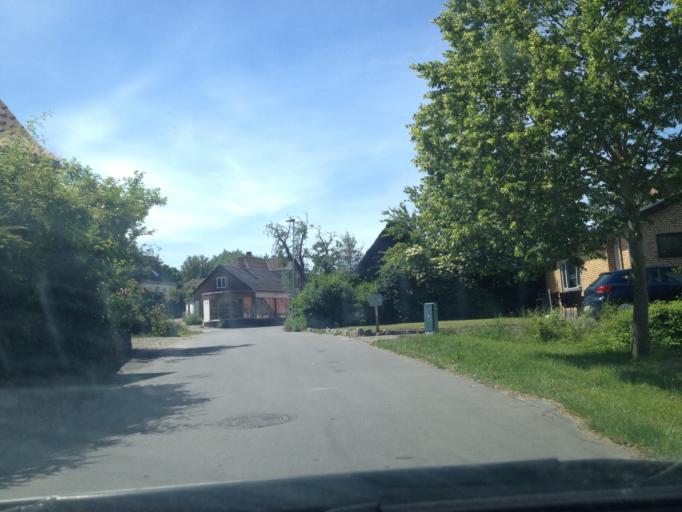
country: DK
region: Central Jutland
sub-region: Samso Kommune
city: Tranebjerg
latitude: 55.8648
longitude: 10.6461
